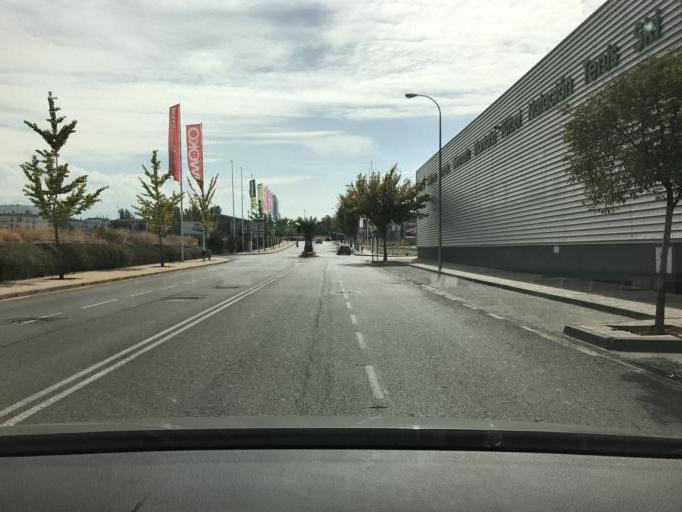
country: ES
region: Andalusia
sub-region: Provincia de Granada
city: Pulianas
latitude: 37.2138
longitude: -3.6152
